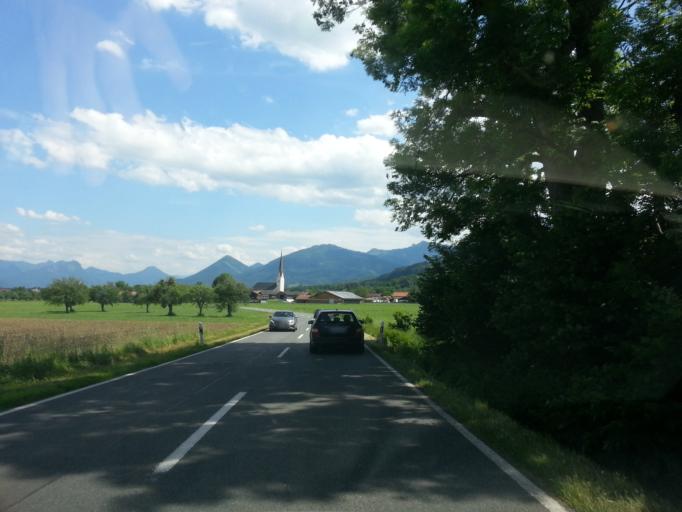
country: DE
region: Bavaria
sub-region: Upper Bavaria
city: Bad Feilnbach
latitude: 47.8008
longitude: 11.9681
